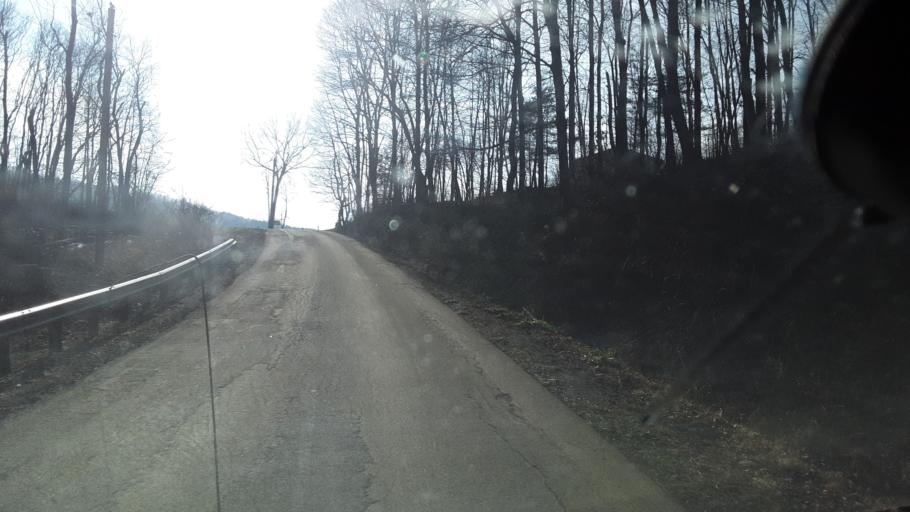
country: US
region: Ohio
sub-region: Knox County
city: Oak Hill
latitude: 40.4218
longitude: -82.1962
